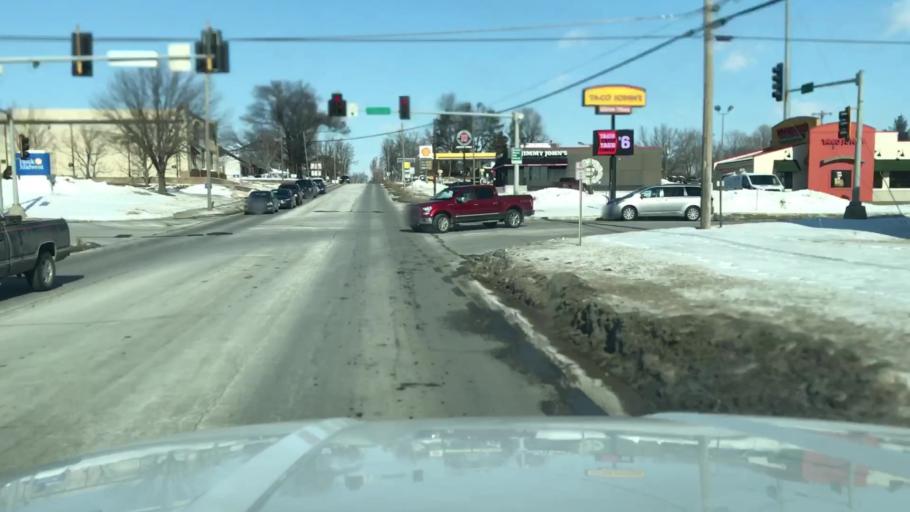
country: US
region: Missouri
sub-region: Nodaway County
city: Maryville
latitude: 40.3344
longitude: -94.8738
